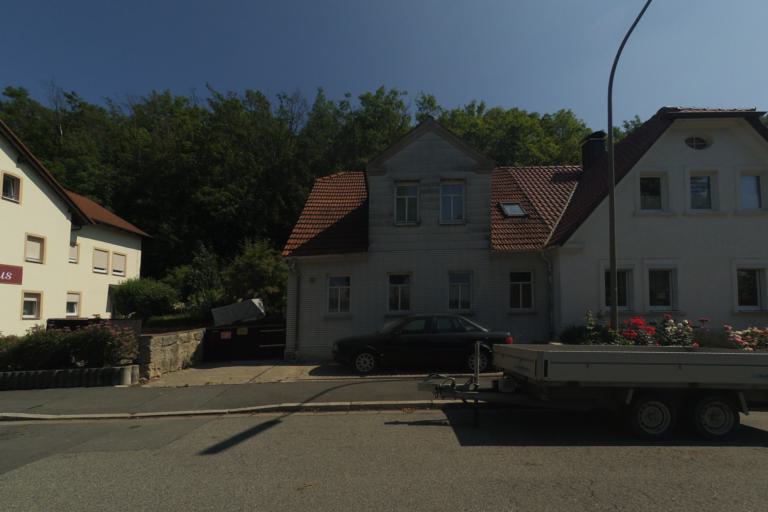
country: DE
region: Bavaria
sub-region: Upper Franconia
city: Burgkunstadt
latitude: 50.1427
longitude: 11.2440
